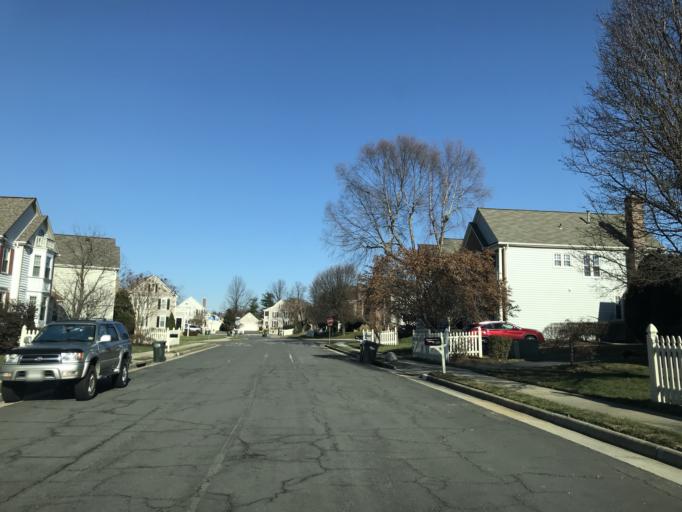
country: US
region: Virginia
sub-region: Fairfax County
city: Franconia
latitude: 38.7763
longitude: -77.1670
